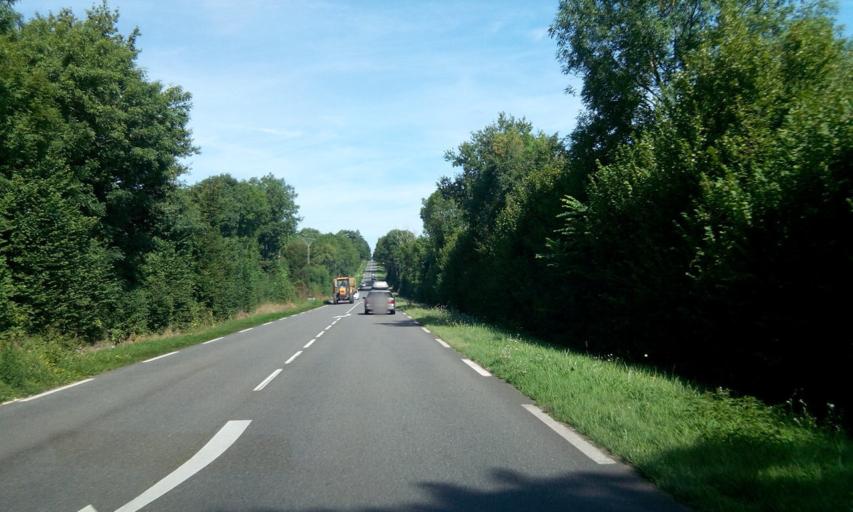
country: FR
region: Poitou-Charentes
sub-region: Departement de la Charente
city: Confolens
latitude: 45.9721
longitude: 0.6907
